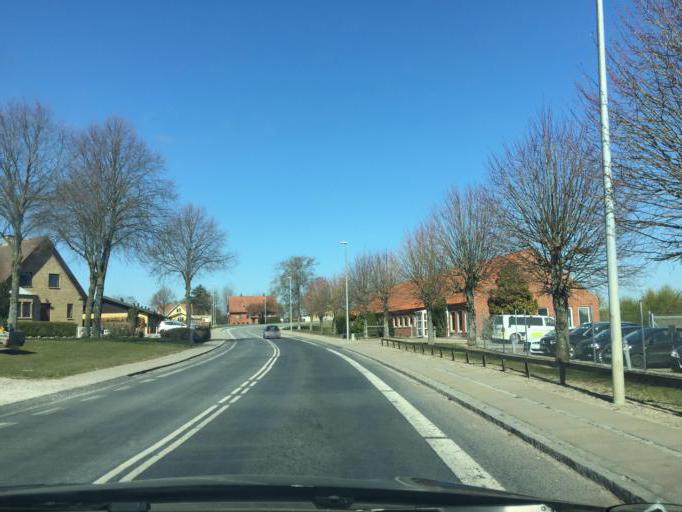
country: DK
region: South Denmark
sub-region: Faaborg-Midtfyn Kommune
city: Ringe
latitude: 55.2428
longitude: 10.4854
